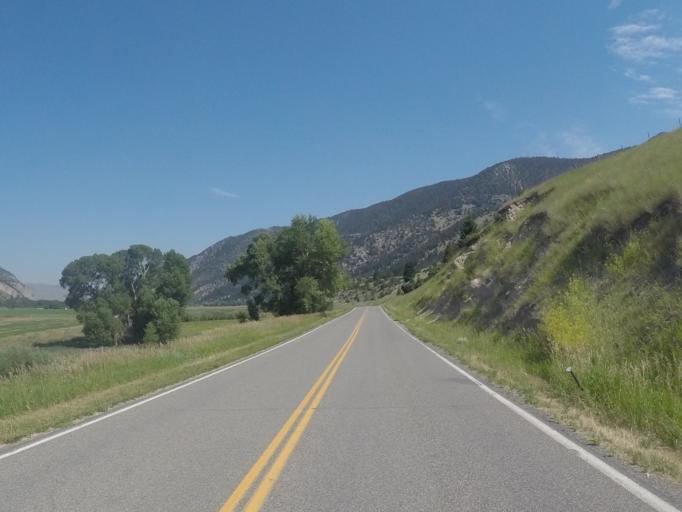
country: US
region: Montana
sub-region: Park County
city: Livingston
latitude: 45.5775
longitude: -110.5637
